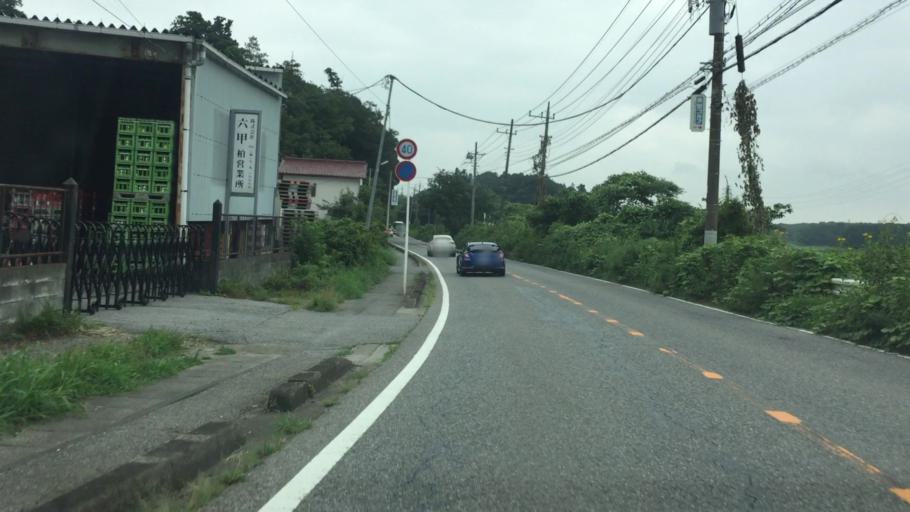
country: JP
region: Chiba
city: Kashiwa
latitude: 35.8261
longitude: 140.0011
